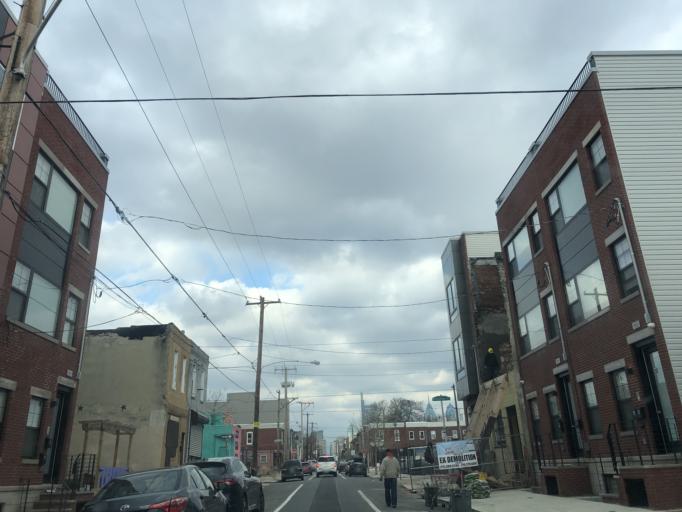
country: US
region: Pennsylvania
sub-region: Philadelphia County
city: Philadelphia
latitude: 39.9309
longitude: -75.1781
